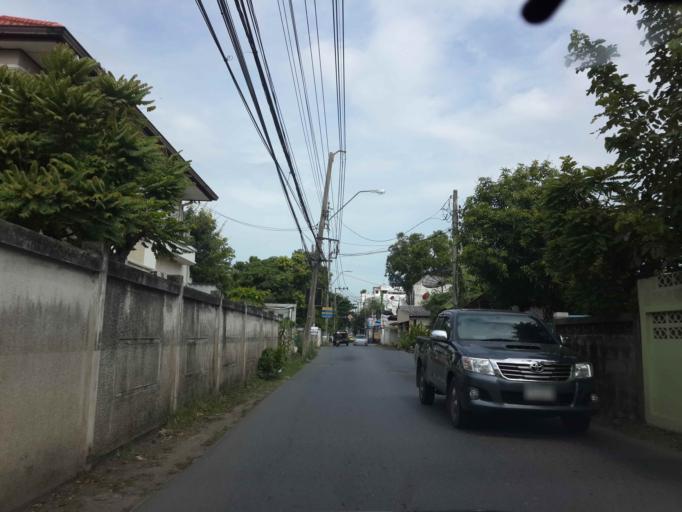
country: TH
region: Bangkok
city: Bang Khen
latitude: 13.8632
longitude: 100.6287
